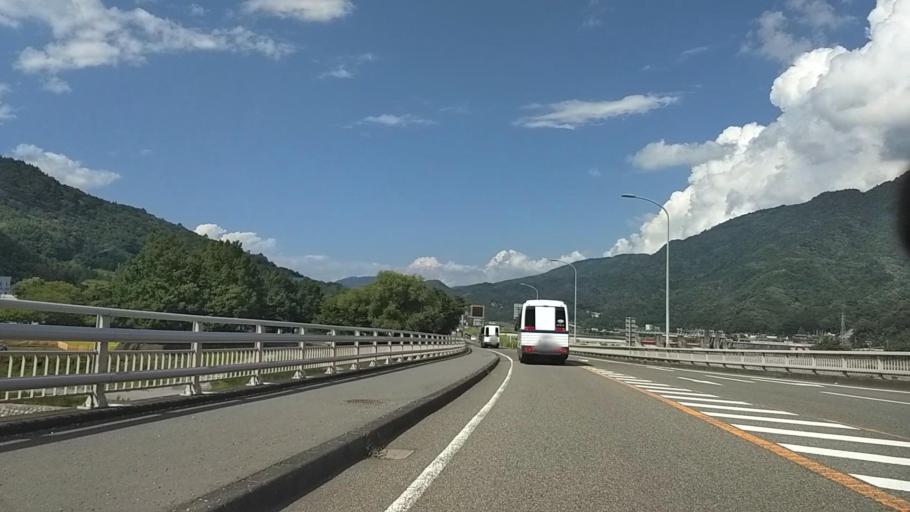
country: JP
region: Shizuoka
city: Fujinomiya
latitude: 35.3708
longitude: 138.4458
